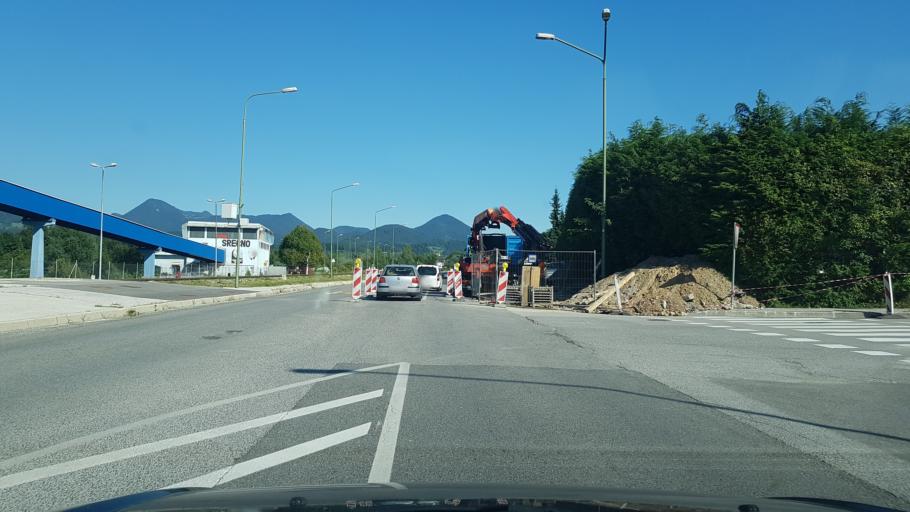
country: SI
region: Velenje
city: Velenje
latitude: 46.3679
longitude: 15.0821
